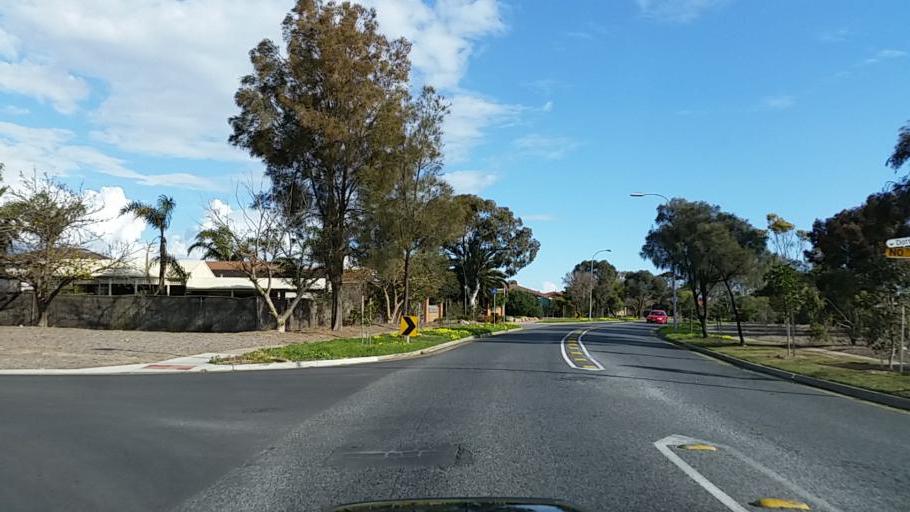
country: AU
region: South Australia
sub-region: Charles Sturt
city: West Lakes Shore
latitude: -34.8574
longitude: 138.4938
